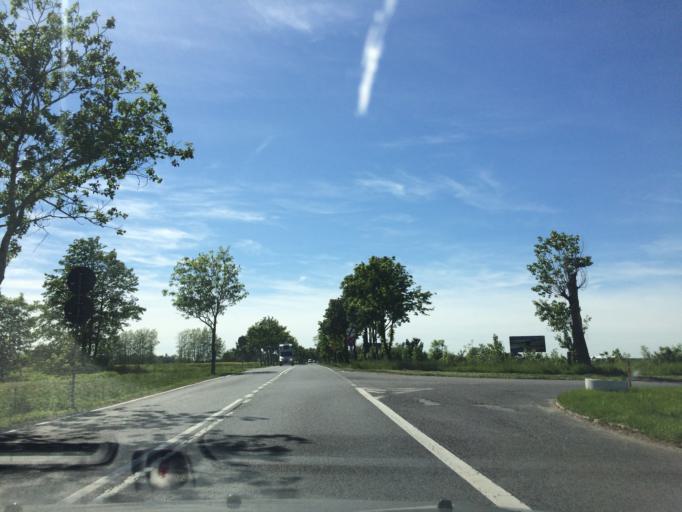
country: PL
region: Lower Silesian Voivodeship
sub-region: Powiat wroclawski
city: Sobotka
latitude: 50.9529
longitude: 16.7768
